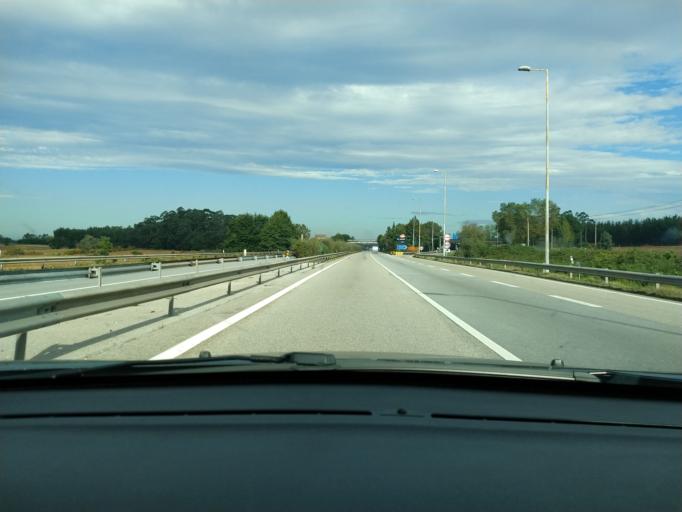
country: PT
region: Aveiro
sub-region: Estarreja
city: Salreu
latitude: 40.7522
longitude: -8.5339
